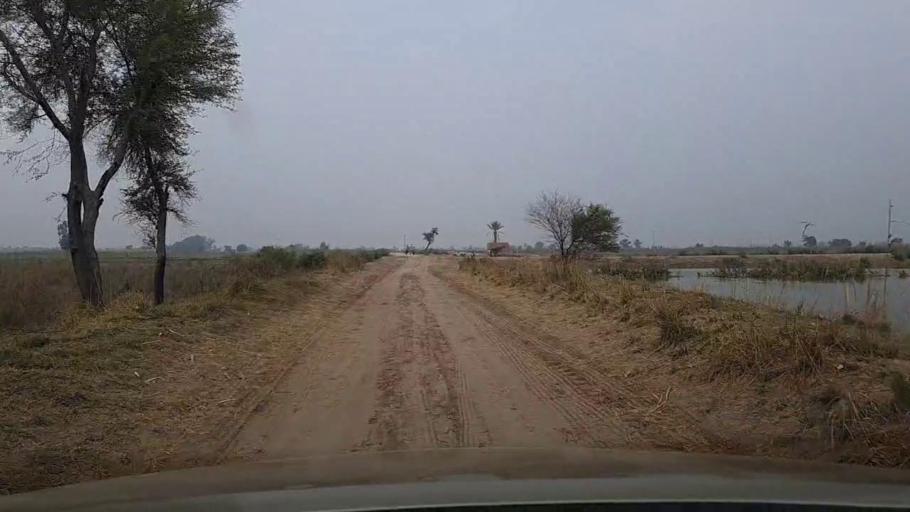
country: PK
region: Sindh
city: Sanghar
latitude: 26.1386
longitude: 68.9265
